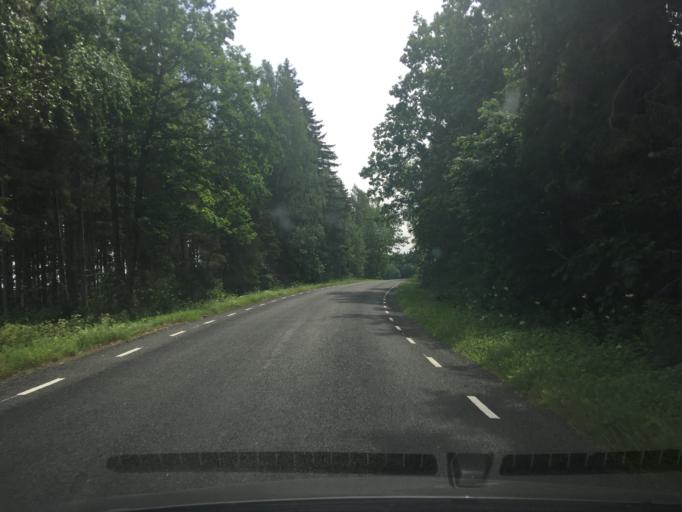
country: EE
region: Raplamaa
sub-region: Kohila vald
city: Kohila
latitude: 59.1132
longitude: 24.8593
